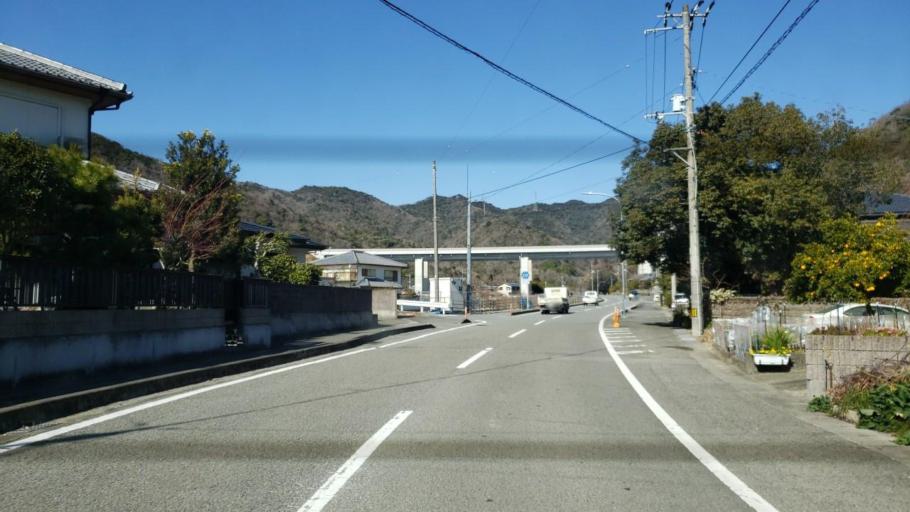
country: JP
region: Tokushima
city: Narutocho-mitsuishi
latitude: 34.1636
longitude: 134.5414
